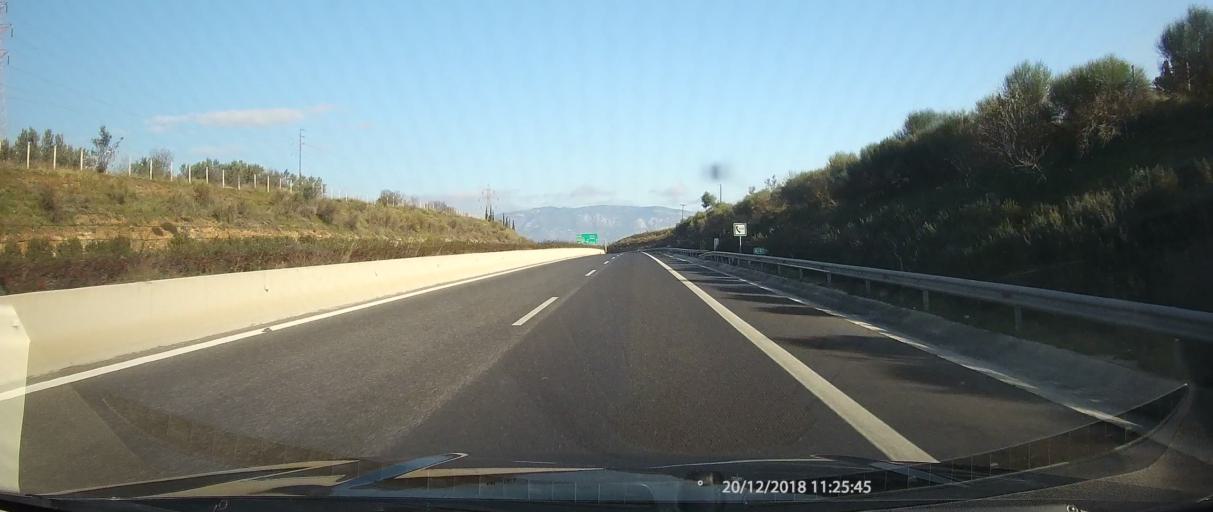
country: GR
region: Peloponnese
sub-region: Nomos Korinthias
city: Arkhaia Korinthos
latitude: 37.9037
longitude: 22.9037
